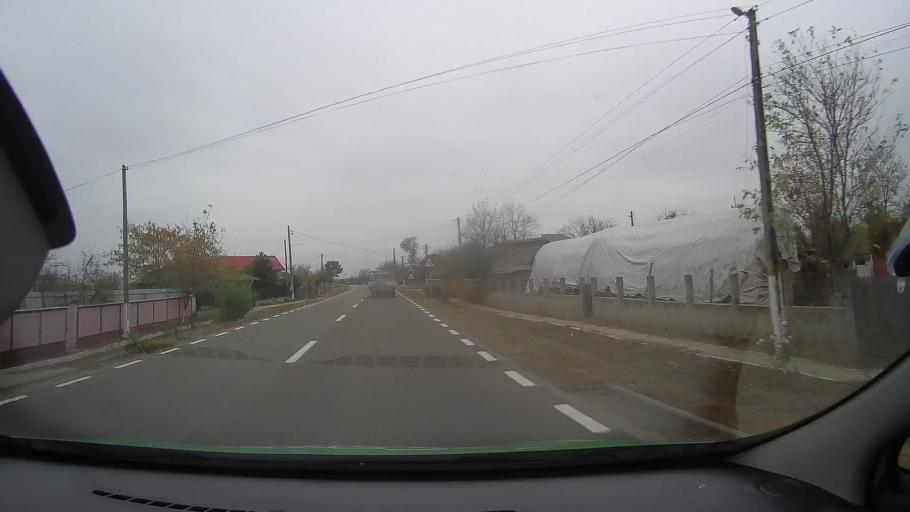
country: RO
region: Ialomita
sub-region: Comuna Scanteia
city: Iazu
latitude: 44.7294
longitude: 27.4262
